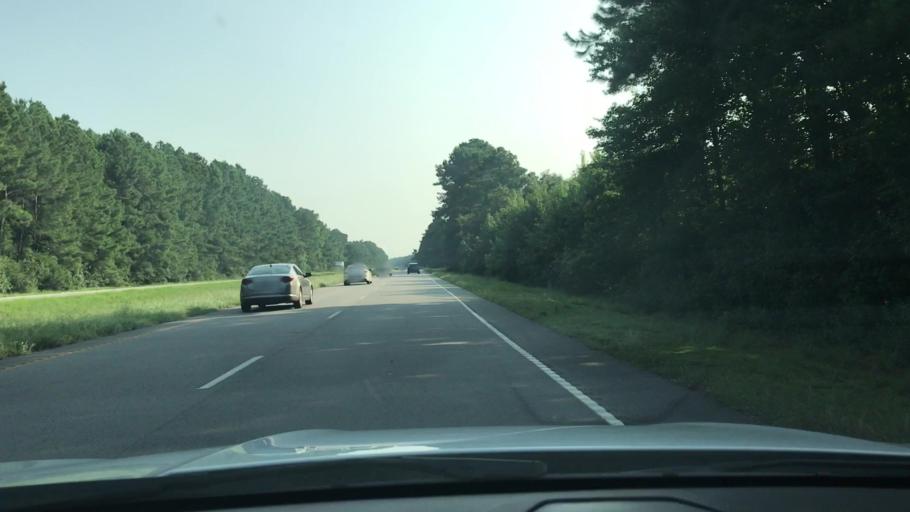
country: US
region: South Carolina
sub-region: Charleston County
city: Awendaw
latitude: 33.1128
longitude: -79.4587
